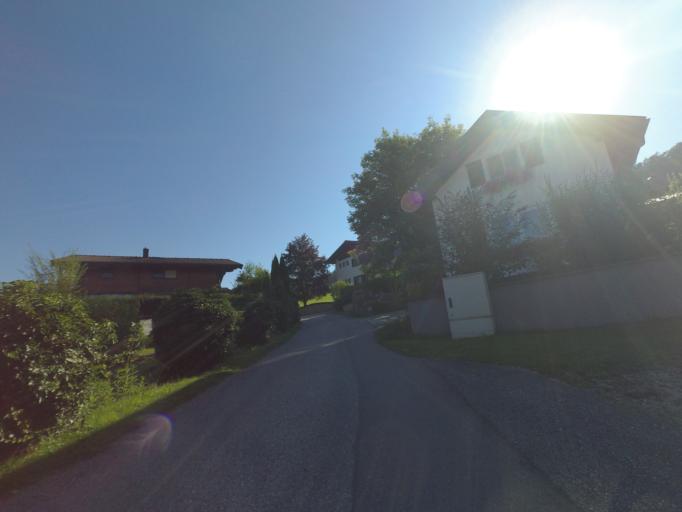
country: AT
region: Salzburg
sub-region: Politischer Bezirk Salzburg-Umgebung
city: Hallwang
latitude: 47.8618
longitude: 13.0966
